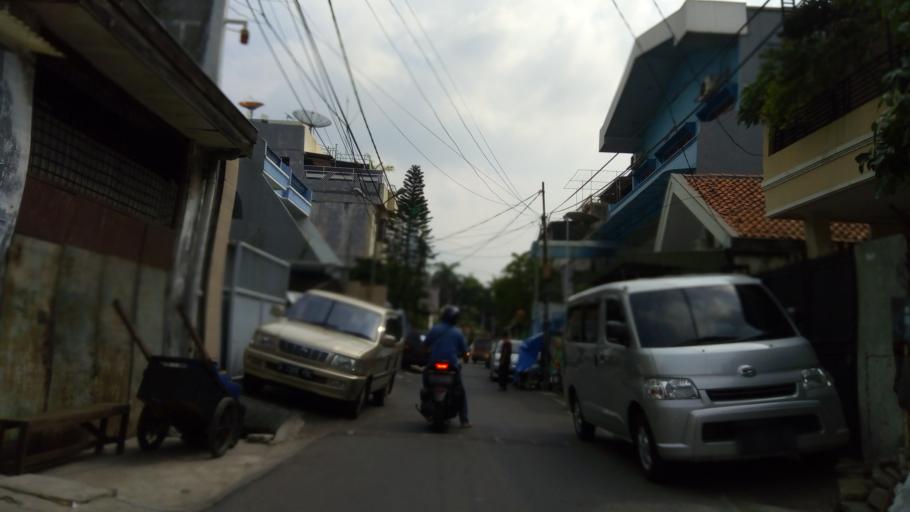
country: ID
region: Jakarta Raya
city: Jakarta
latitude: -6.1589
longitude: 106.8353
